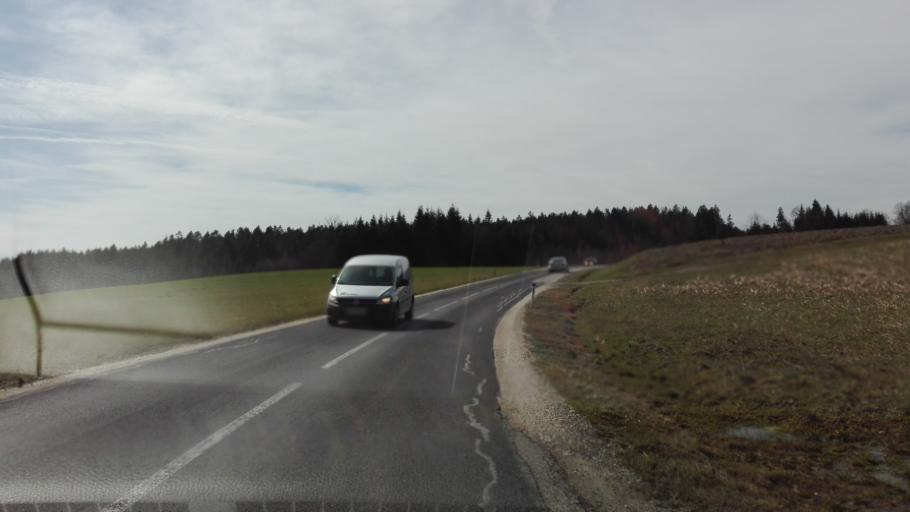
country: AT
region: Upper Austria
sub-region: Politischer Bezirk Scharding
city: Sankt Marienkirchen bei Schaerding
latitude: 48.3749
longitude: 13.6257
